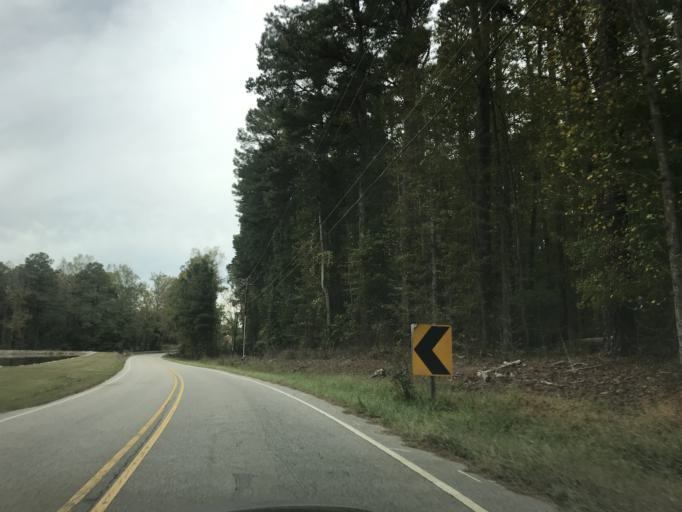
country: US
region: North Carolina
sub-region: Wake County
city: Knightdale
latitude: 35.8324
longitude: -78.5143
